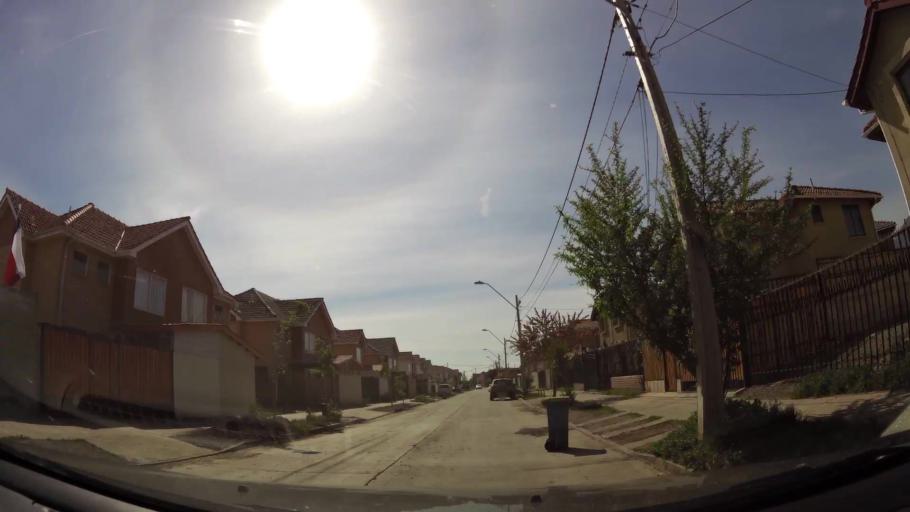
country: CL
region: Santiago Metropolitan
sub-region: Provincia de Cordillera
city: Puente Alto
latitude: -33.5971
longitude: -70.5422
